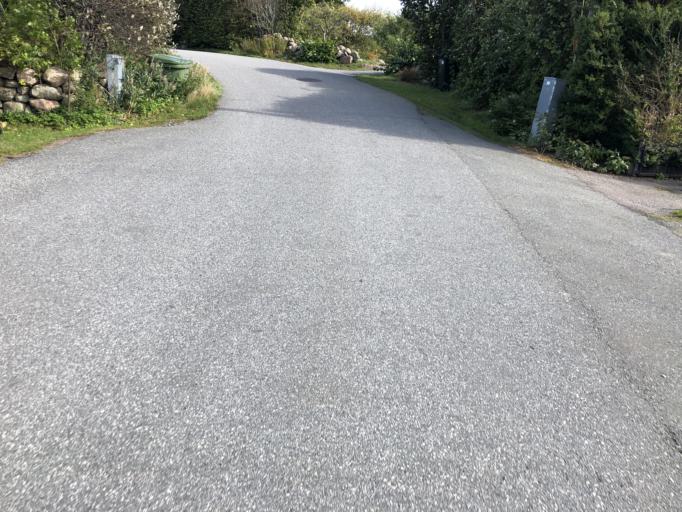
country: SE
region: Vaestra Goetaland
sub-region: Goteborg
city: Torslanda
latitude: 57.7447
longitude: 11.8168
